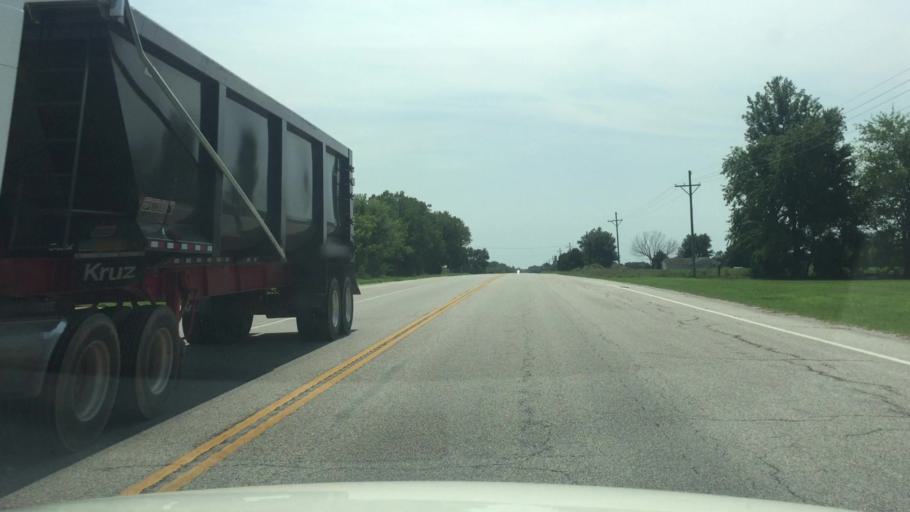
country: US
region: Kansas
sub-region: Cherokee County
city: Galena
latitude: 37.1043
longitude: -94.7044
